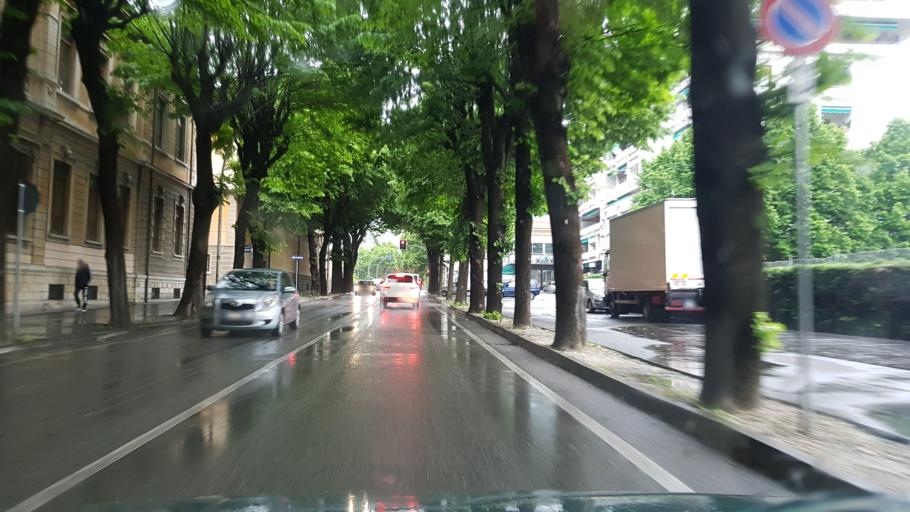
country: IT
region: Veneto
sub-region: Provincia di Treviso
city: Vittorio Veneto
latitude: 45.9892
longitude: 12.2991
